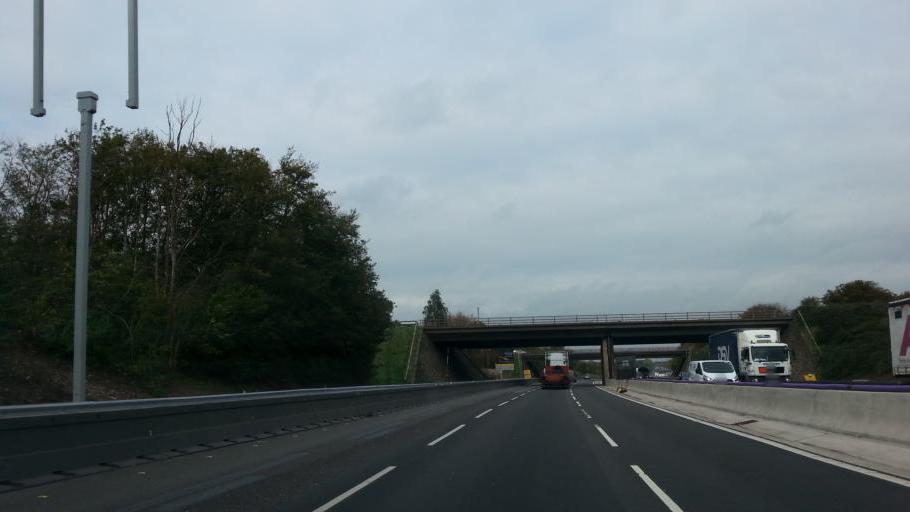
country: GB
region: England
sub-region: Cheshire East
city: Holmes Chapel
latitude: 53.1990
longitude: -2.3871
